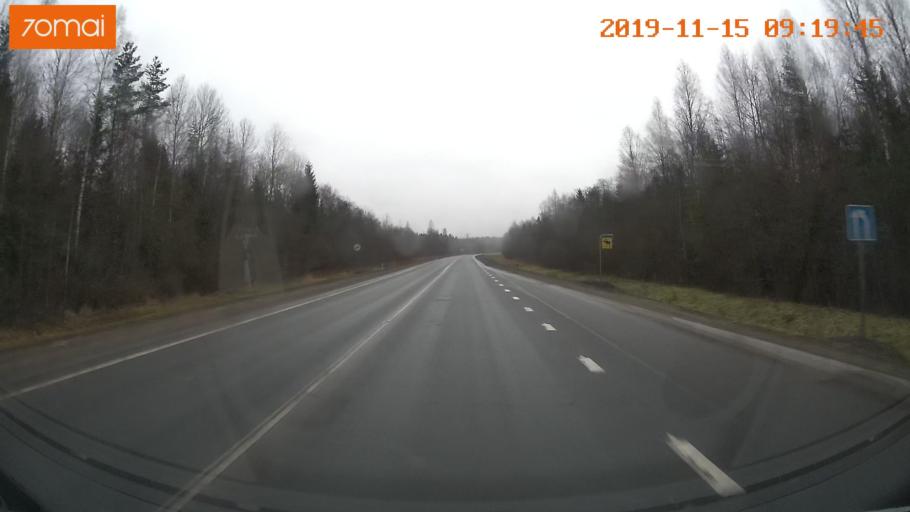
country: RU
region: Vologda
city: Tonshalovo
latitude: 59.2863
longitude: 38.0220
